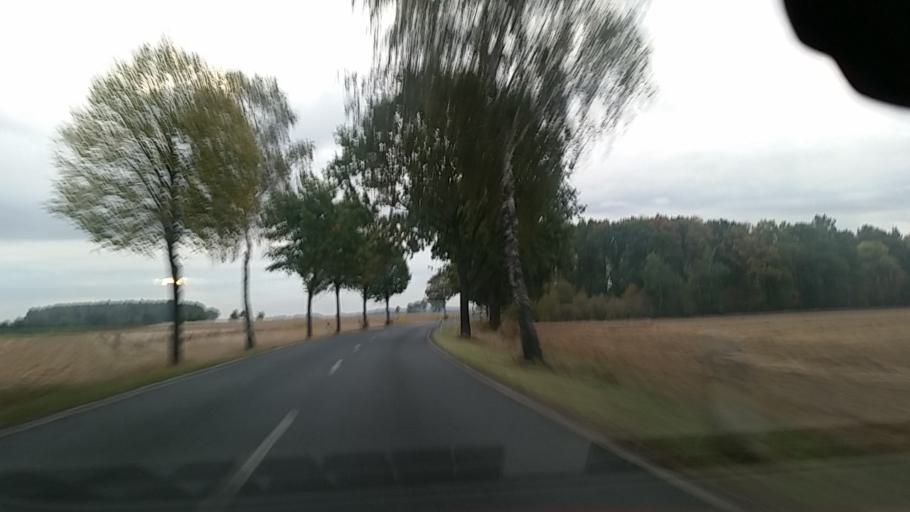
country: DE
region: Lower Saxony
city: Hankensbuttel
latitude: 52.7452
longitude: 10.5595
